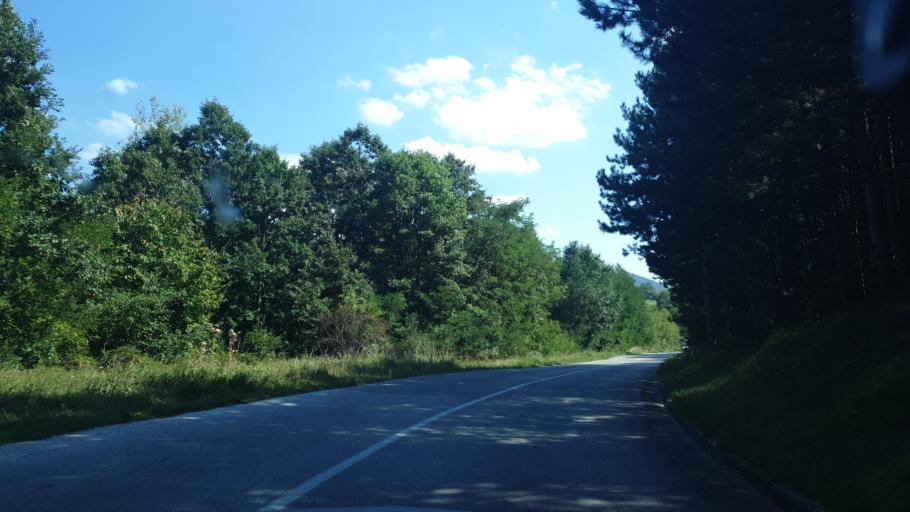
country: RS
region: Central Serbia
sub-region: Zlatiborski Okrug
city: Kosjeric
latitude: 44.0271
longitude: 20.0172
